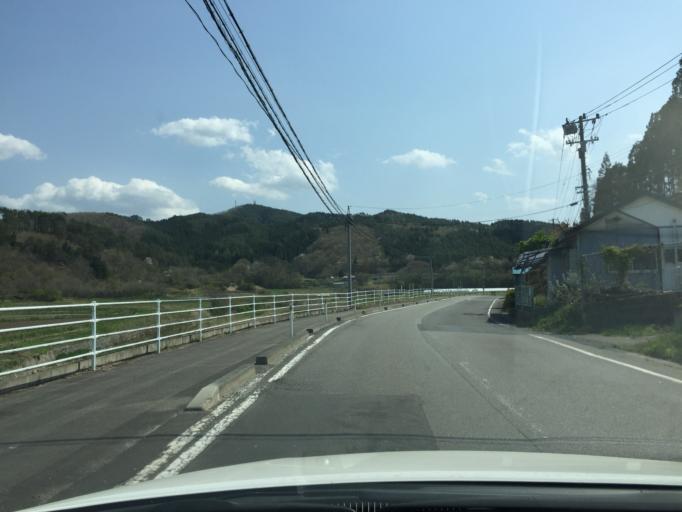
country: JP
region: Fukushima
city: Namie
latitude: 37.4332
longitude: 140.7955
